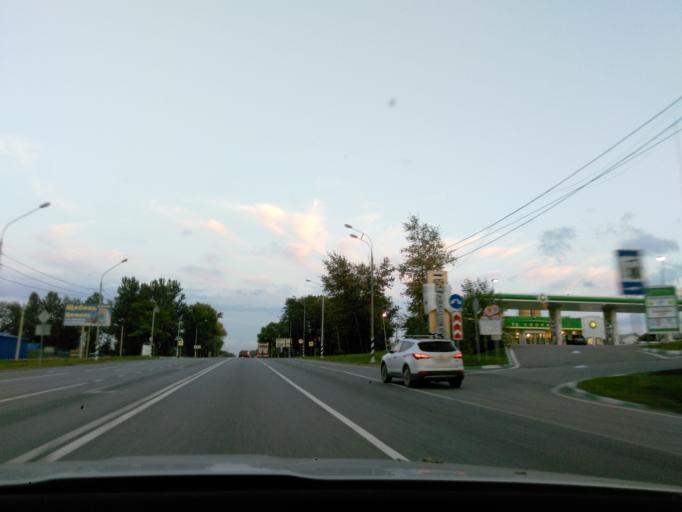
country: RU
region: Moskovskaya
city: Klin
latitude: 56.3505
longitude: 36.7039
